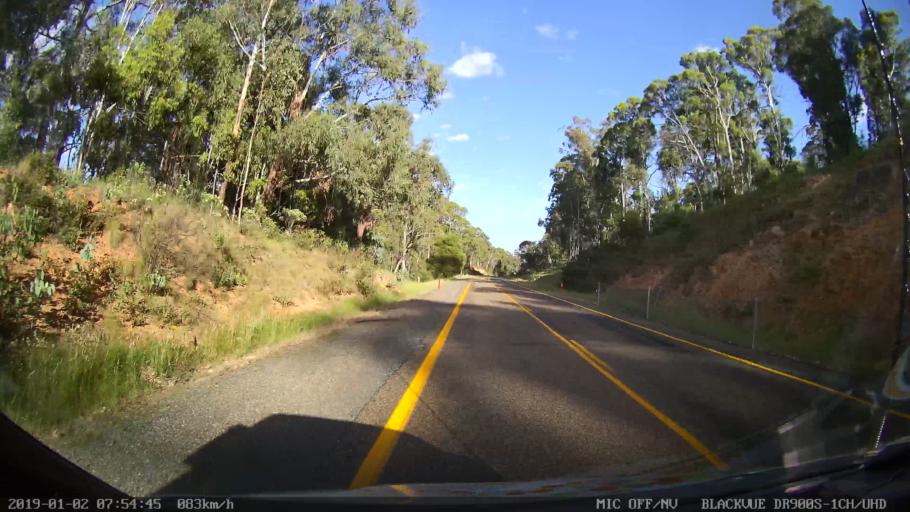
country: AU
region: New South Wales
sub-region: Tumut Shire
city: Tumut
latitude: -35.6921
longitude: 148.4934
